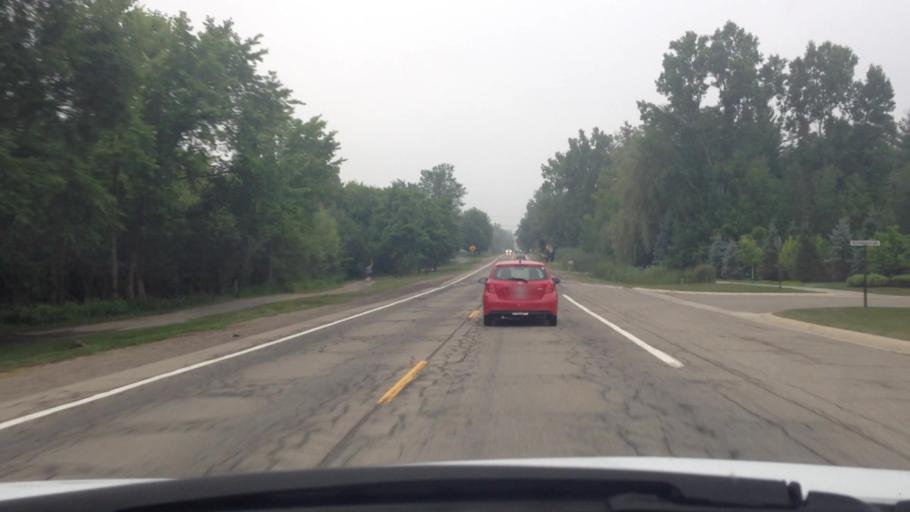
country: US
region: Michigan
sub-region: Oakland County
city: Clarkston
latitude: 42.7382
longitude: -83.3501
